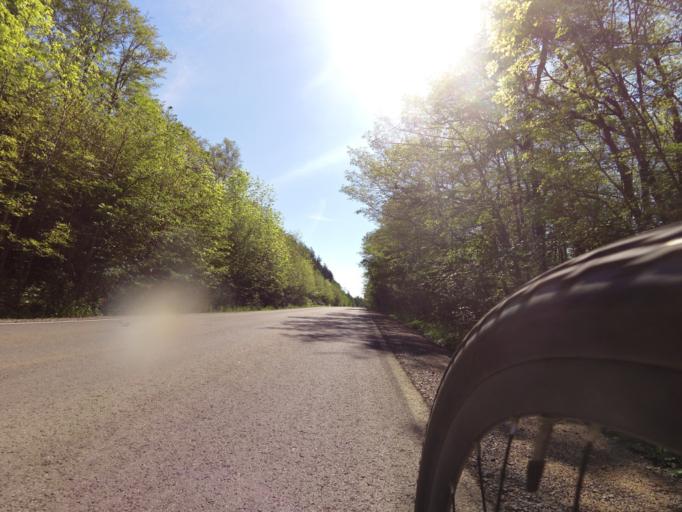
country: CA
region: Quebec
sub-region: Laurentides
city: Brownsburg-Chatham
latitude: 45.8455
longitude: -74.5232
